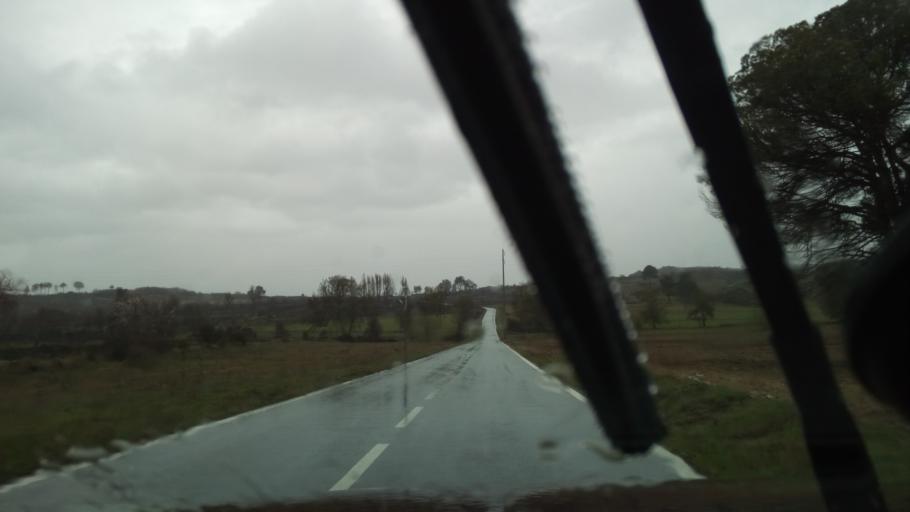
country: PT
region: Guarda
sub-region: Fornos de Algodres
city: Fornos de Algodres
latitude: 40.5560
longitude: -7.5220
